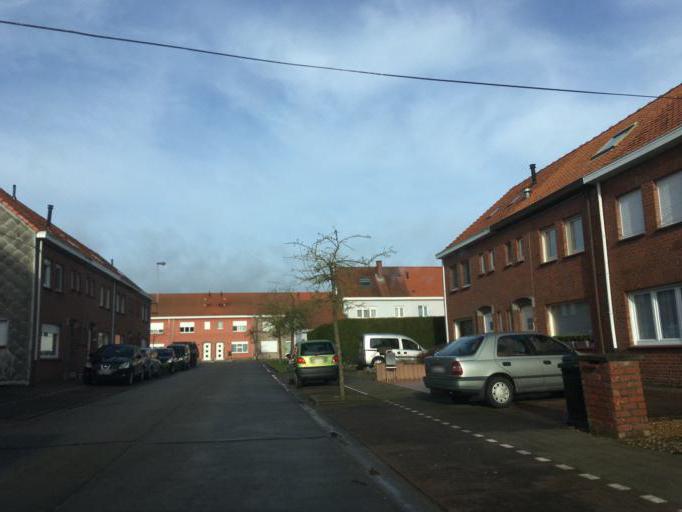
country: BE
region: Flanders
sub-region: Provincie West-Vlaanderen
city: Roeselare
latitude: 50.9385
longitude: 3.1066
